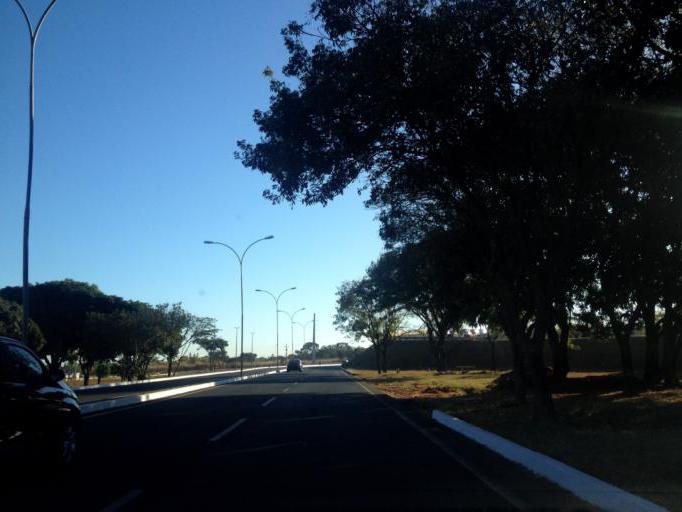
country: BR
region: Federal District
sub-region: Brasilia
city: Brasilia
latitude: -15.7761
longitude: -47.9396
